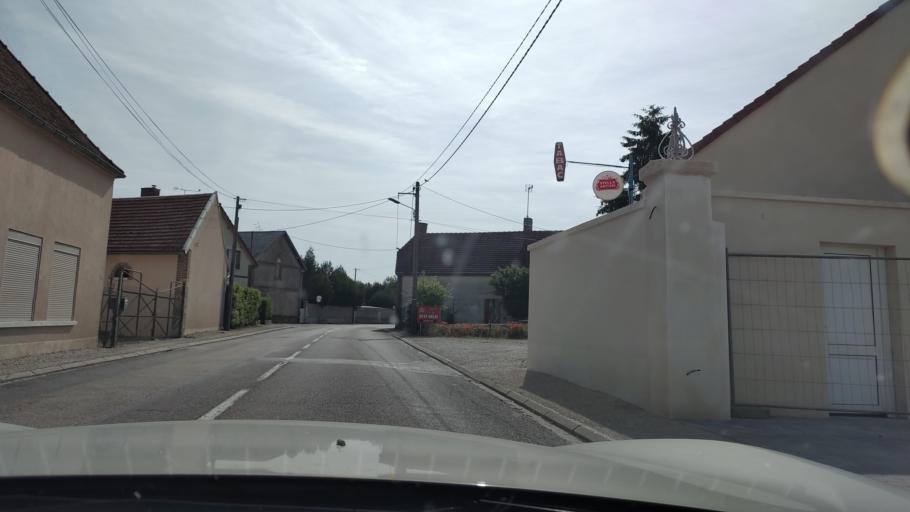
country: FR
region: Champagne-Ardenne
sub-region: Departement de l'Aube
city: Marigny-le-Chatel
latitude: 48.4032
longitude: 3.7598
